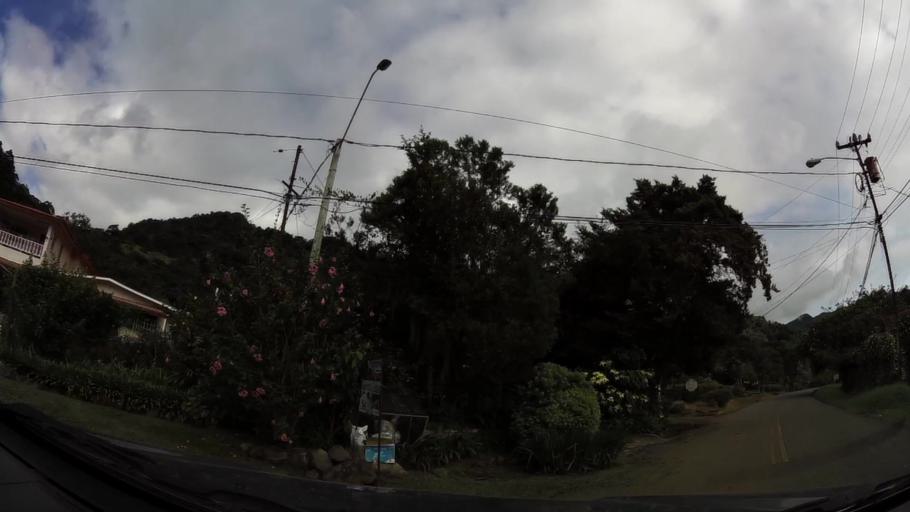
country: PA
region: Chiriqui
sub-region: Distrito Boquete
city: Boquete
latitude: 8.7993
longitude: -82.4370
